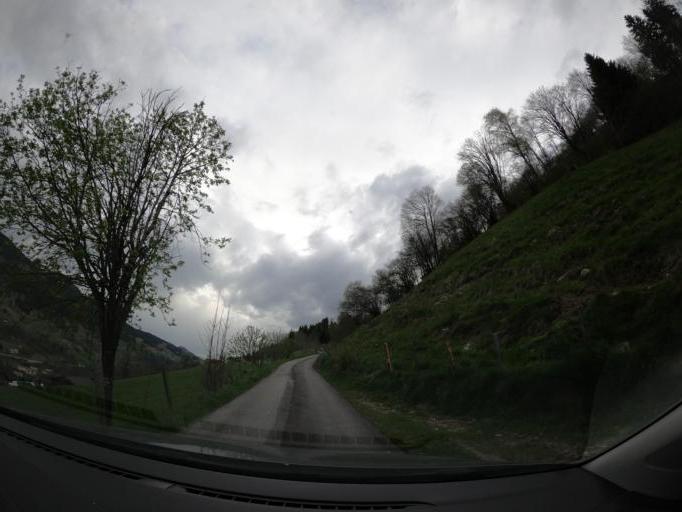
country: AT
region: Salzburg
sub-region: Politischer Bezirk Zell am See
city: Lend
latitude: 47.3018
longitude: 13.0655
